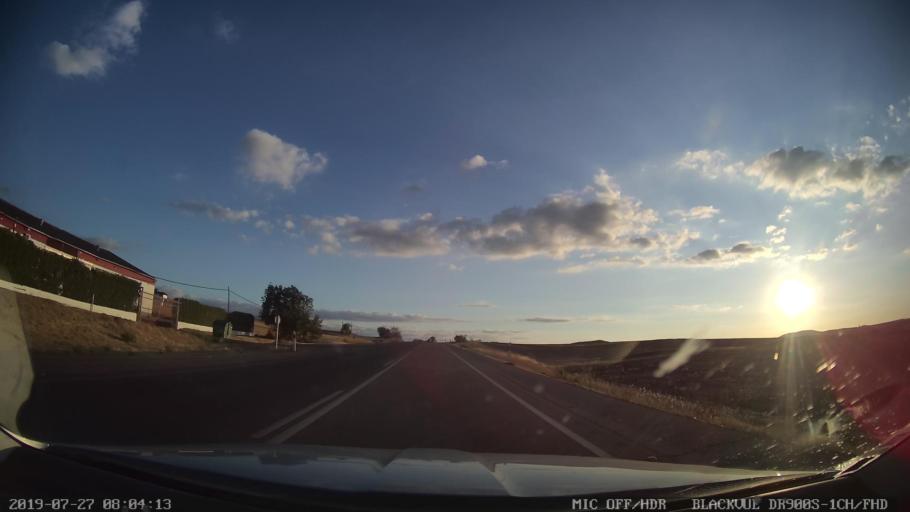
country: ES
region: Extremadura
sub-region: Provincia de Badajoz
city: Merida
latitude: 38.9337
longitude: -6.3119
